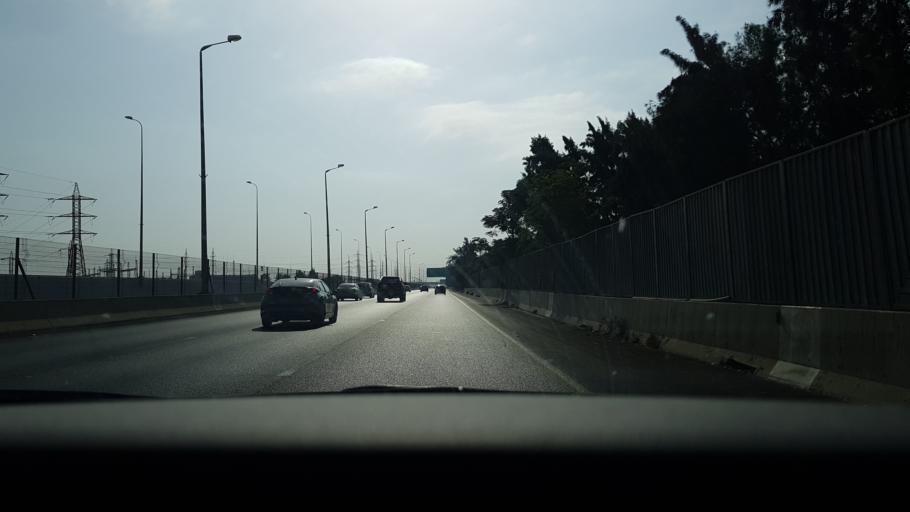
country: IL
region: Tel Aviv
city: Azor
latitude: 32.0280
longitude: 34.8075
